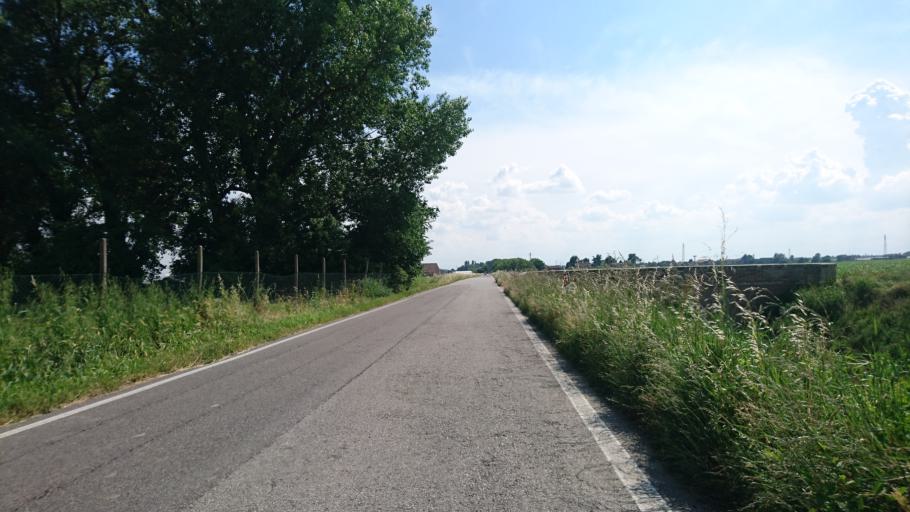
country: IT
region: Veneto
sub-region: Provincia di Rovigo
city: Castelmassa
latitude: 45.0451
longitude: 11.3218
